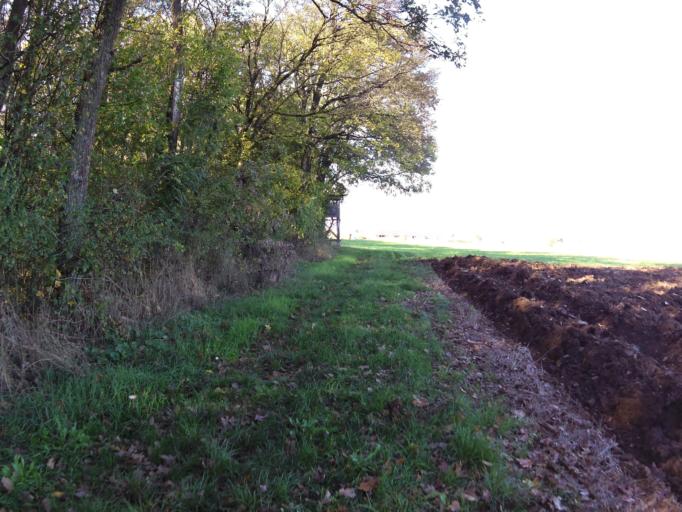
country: DE
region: Bavaria
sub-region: Regierungsbezirk Unterfranken
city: Sulzfeld am Main
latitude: 49.7226
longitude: 10.0931
